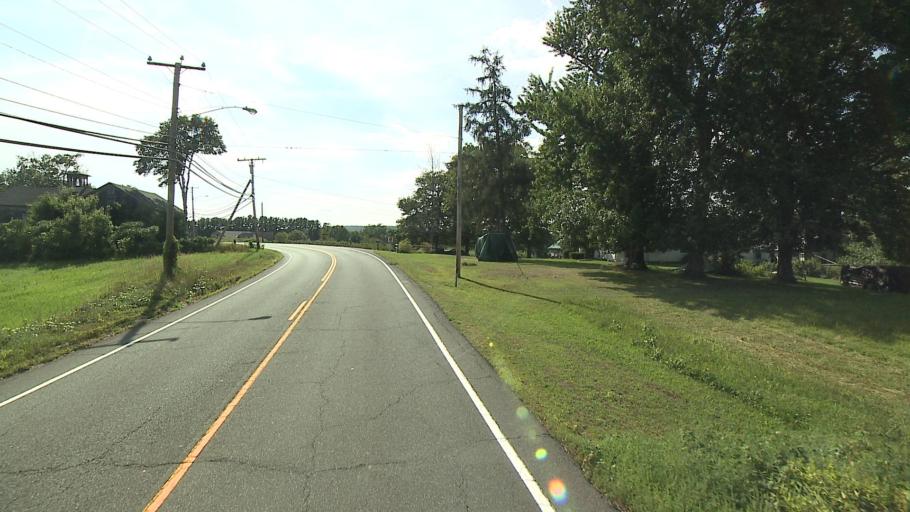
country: US
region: Connecticut
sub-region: Hartford County
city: Farmington
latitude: 41.7669
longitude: -72.8686
